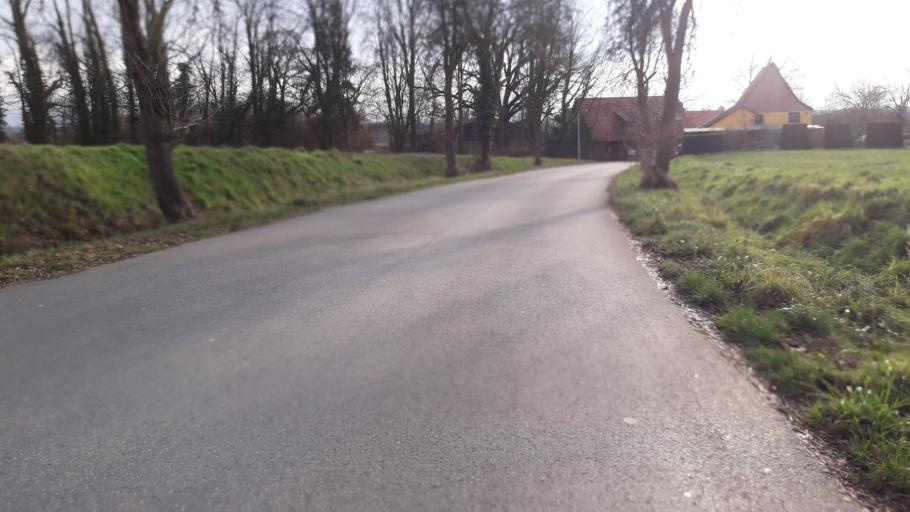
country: DE
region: North Rhine-Westphalia
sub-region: Regierungsbezirk Arnsberg
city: Welver
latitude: 51.5653
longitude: 7.9740
